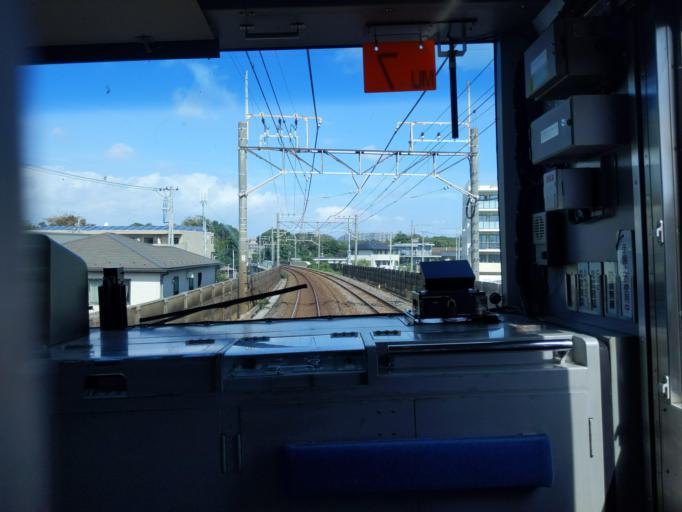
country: JP
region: Chiba
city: Funabashi
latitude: 35.7213
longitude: 139.9679
